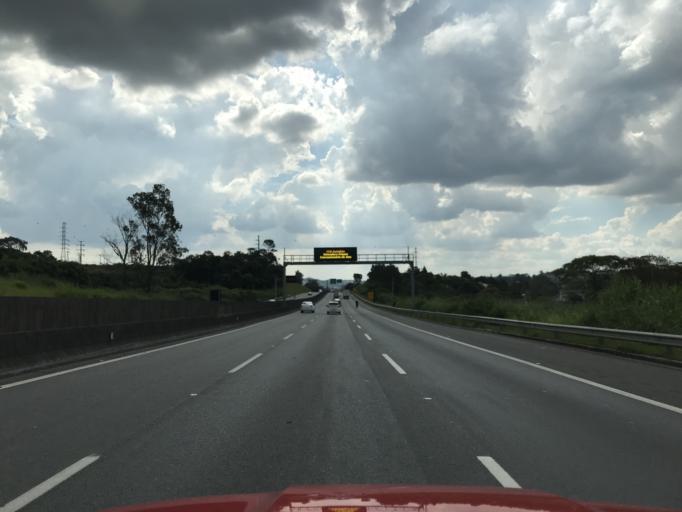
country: BR
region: Sao Paulo
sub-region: Louveira
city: Louveira
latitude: -23.0727
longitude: -46.9851
